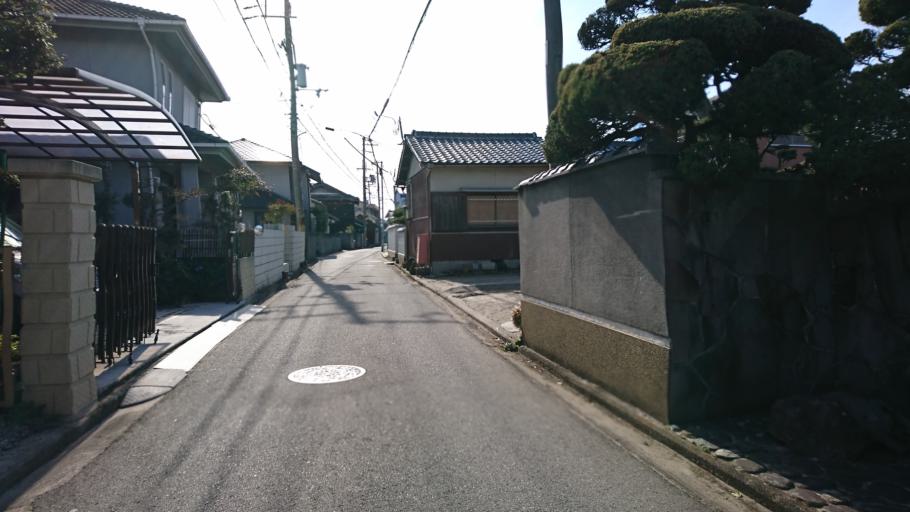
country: JP
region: Hyogo
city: Kakogawacho-honmachi
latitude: 34.7809
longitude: 134.8364
